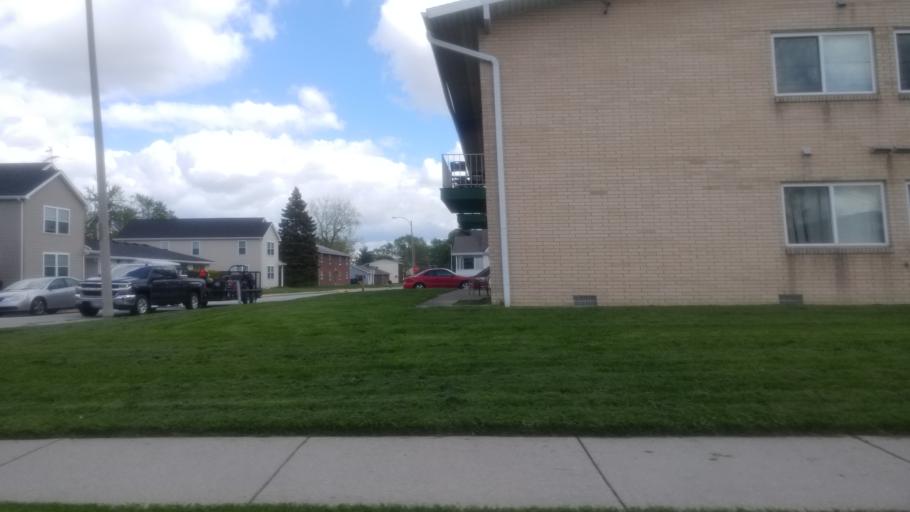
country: US
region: Ohio
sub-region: Wood County
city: Bowling Green
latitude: 41.3684
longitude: -83.6433
